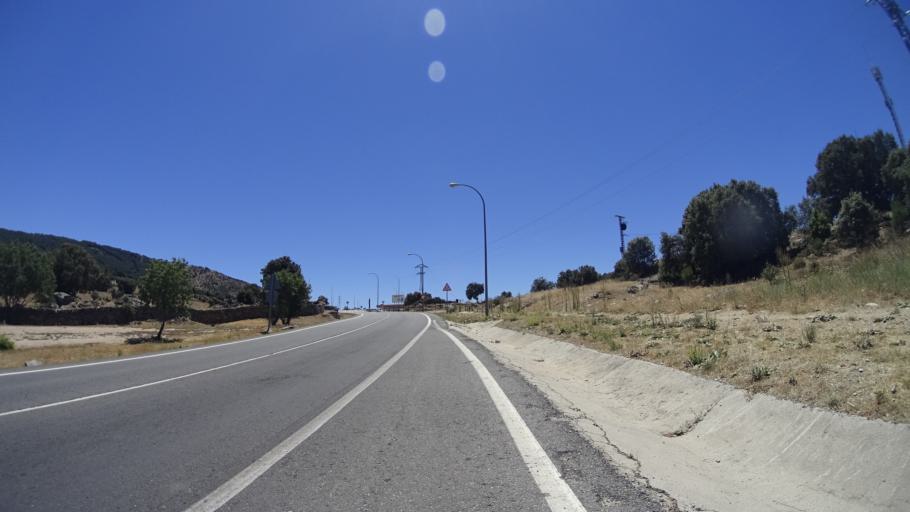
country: ES
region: Madrid
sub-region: Provincia de Madrid
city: Collado Mediano
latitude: 40.6871
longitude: -4.0168
